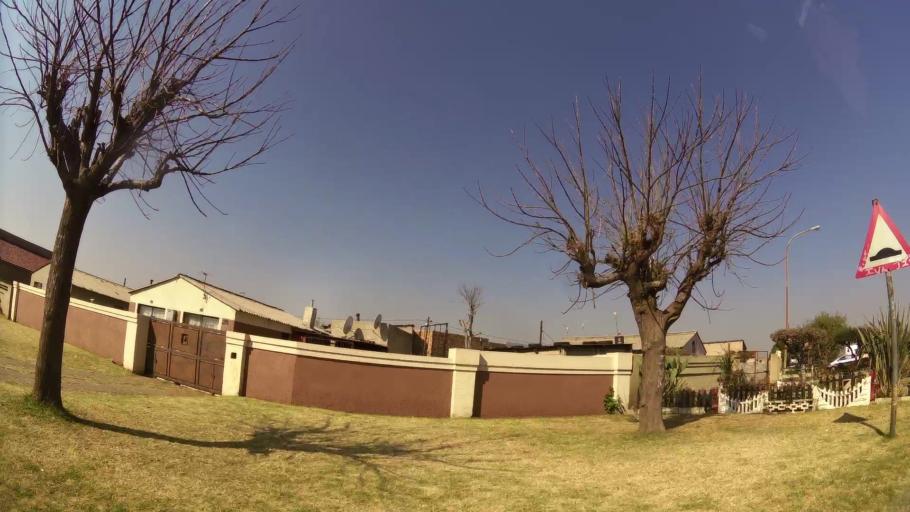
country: ZA
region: Gauteng
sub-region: Ekurhuleni Metropolitan Municipality
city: Benoni
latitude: -26.2222
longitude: 28.3029
